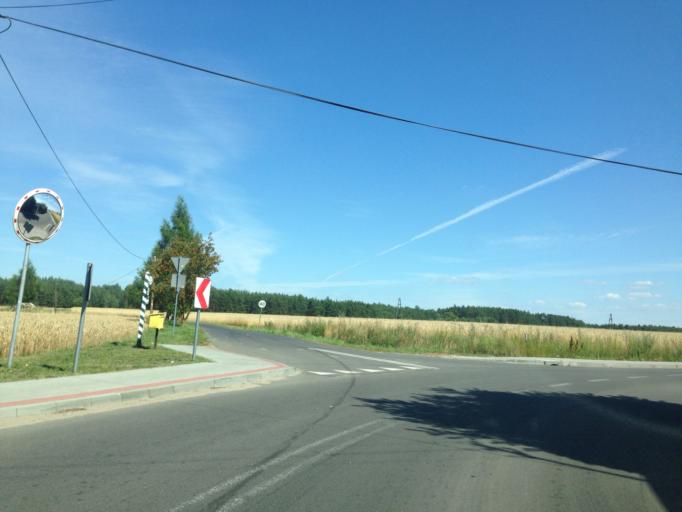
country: PL
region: Kujawsko-Pomorskie
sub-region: Powiat tucholski
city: Sliwice
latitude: 53.6397
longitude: 18.2275
